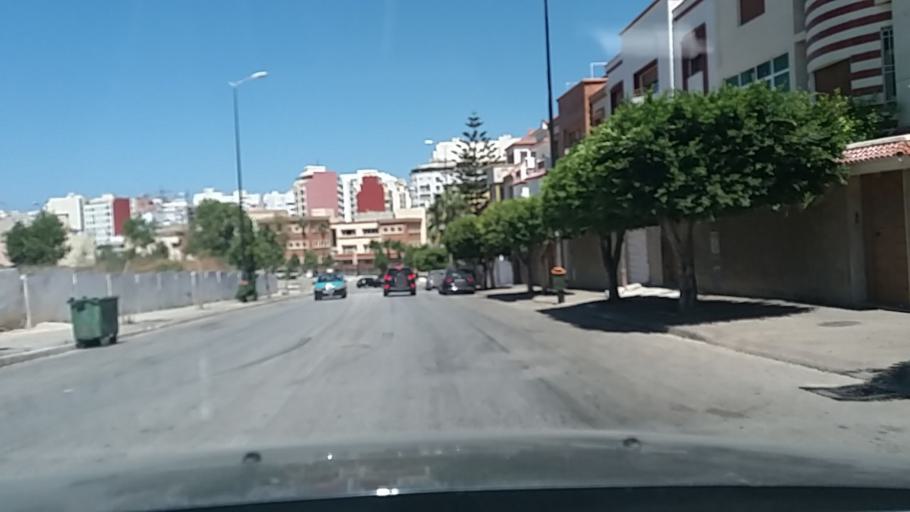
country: MA
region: Tanger-Tetouan
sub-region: Tanger-Assilah
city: Tangier
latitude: 35.7697
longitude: -5.7940
